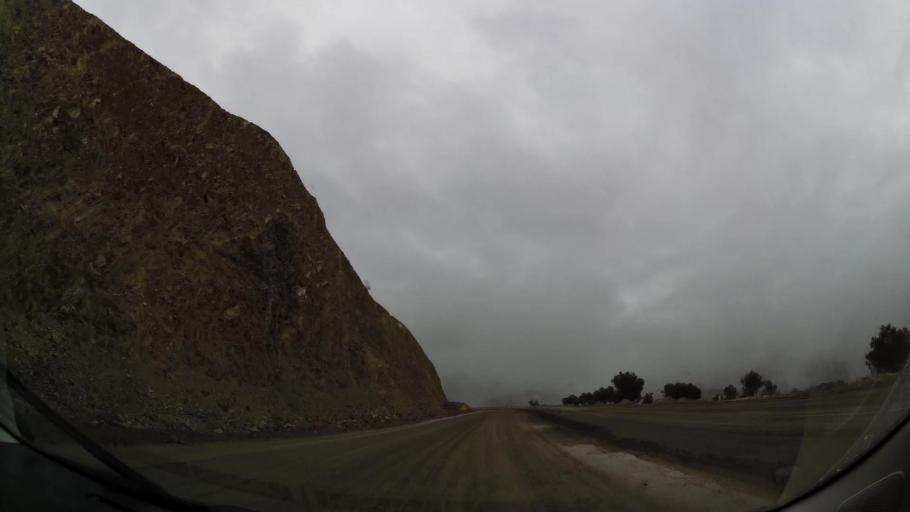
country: MA
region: Taza-Al Hoceima-Taounate
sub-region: Taza
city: Ajdir
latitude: 34.8992
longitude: -3.7840
